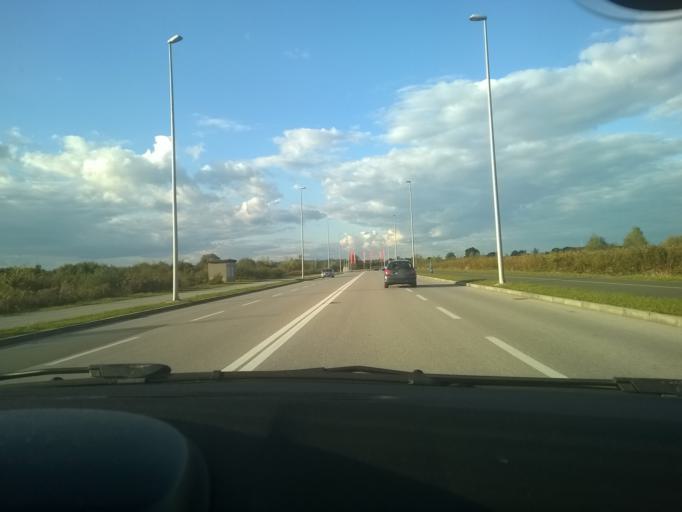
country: HR
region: Zagrebacka
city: Zapresic
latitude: 45.8750
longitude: 15.8246
